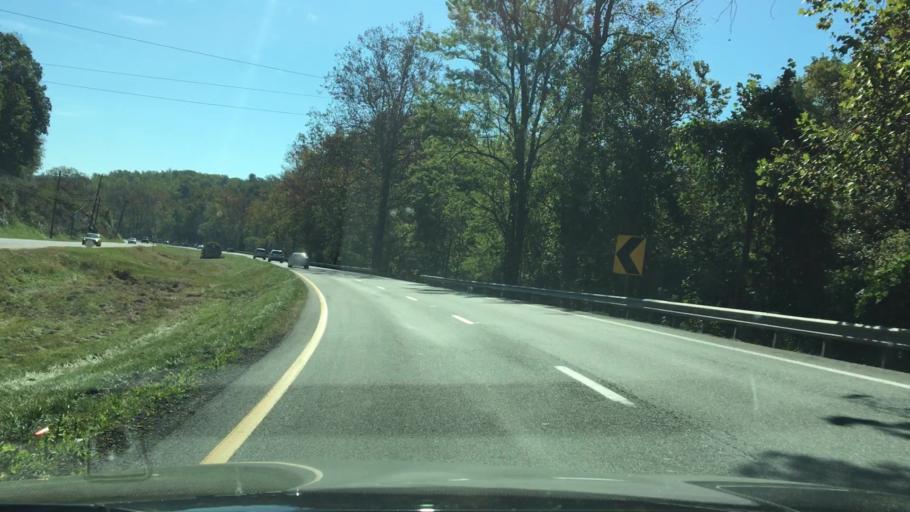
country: US
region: Virginia
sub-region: Roanoke County
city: Narrows
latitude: 37.1332
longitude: -79.9724
